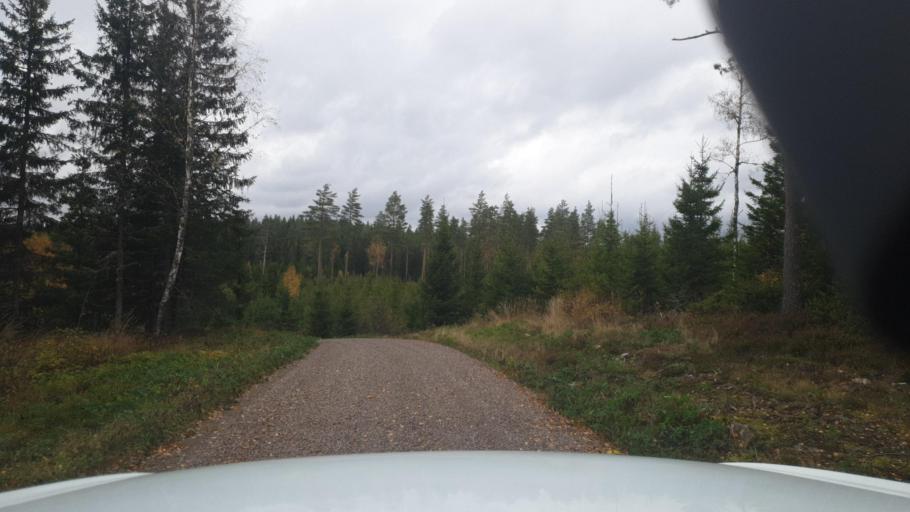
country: SE
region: Vaermland
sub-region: Torsby Kommun
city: Torsby
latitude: 59.9466
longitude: 12.7947
